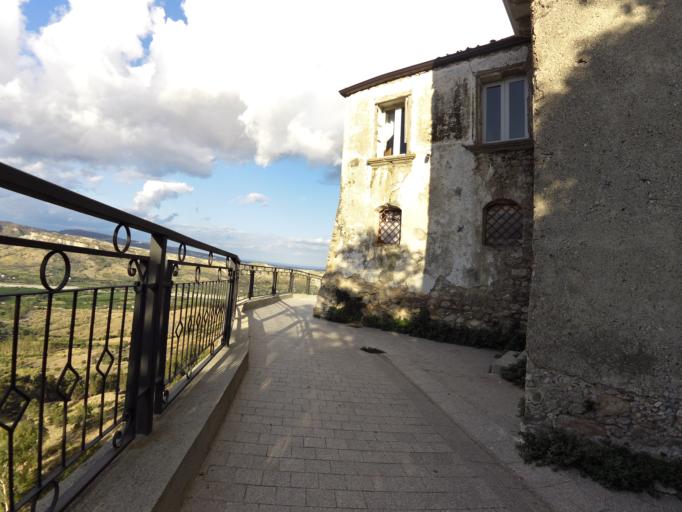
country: IT
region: Calabria
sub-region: Provincia di Reggio Calabria
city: Caulonia
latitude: 38.3832
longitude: 16.4068
